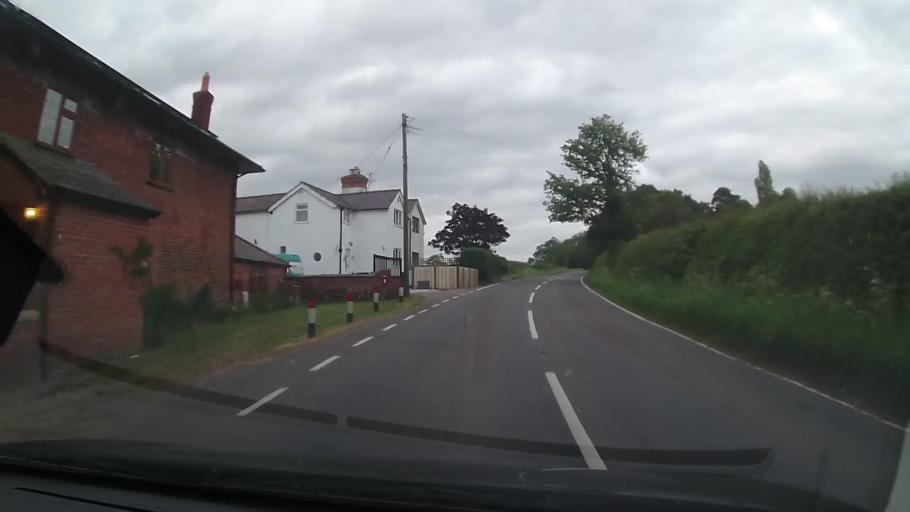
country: GB
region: England
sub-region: Shropshire
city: Clive
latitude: 52.8247
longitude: -2.7379
